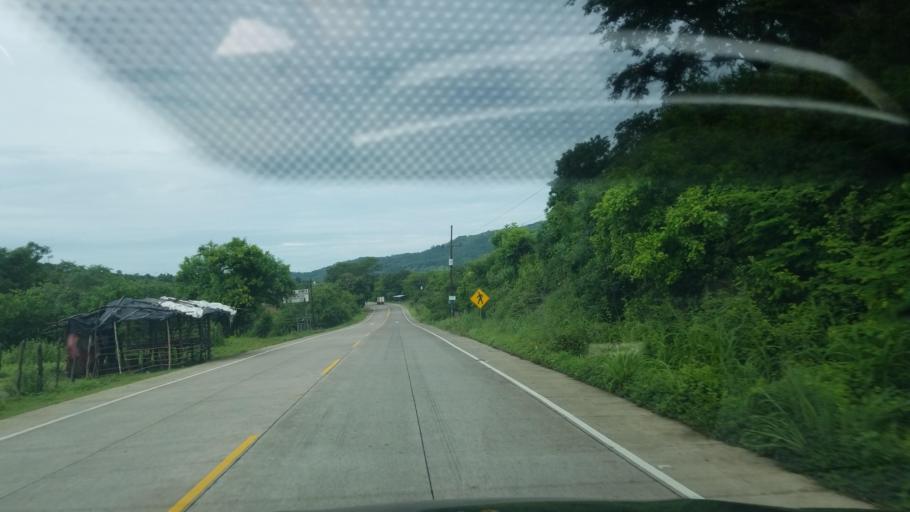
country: HN
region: Choluteca
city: Pespire
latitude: 13.6602
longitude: -87.3629
